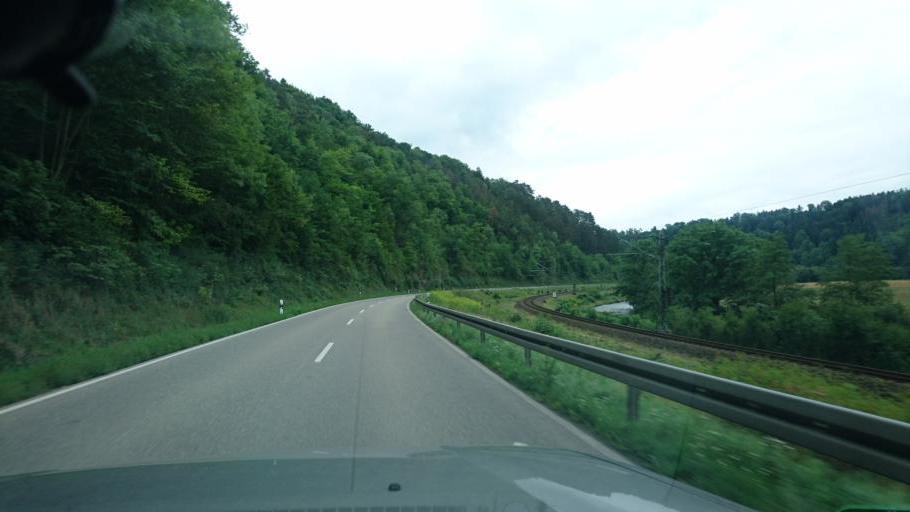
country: DE
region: Baden-Wuerttemberg
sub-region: Freiburg Region
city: Sulz am Neckar
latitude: 48.3736
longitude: 8.6573
